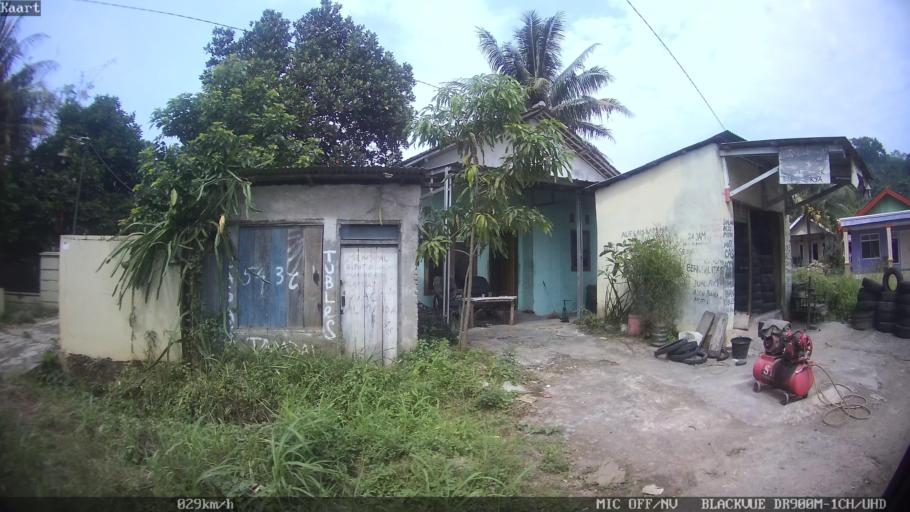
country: ID
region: Lampung
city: Bandarlampung
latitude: -5.4533
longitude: 105.2437
